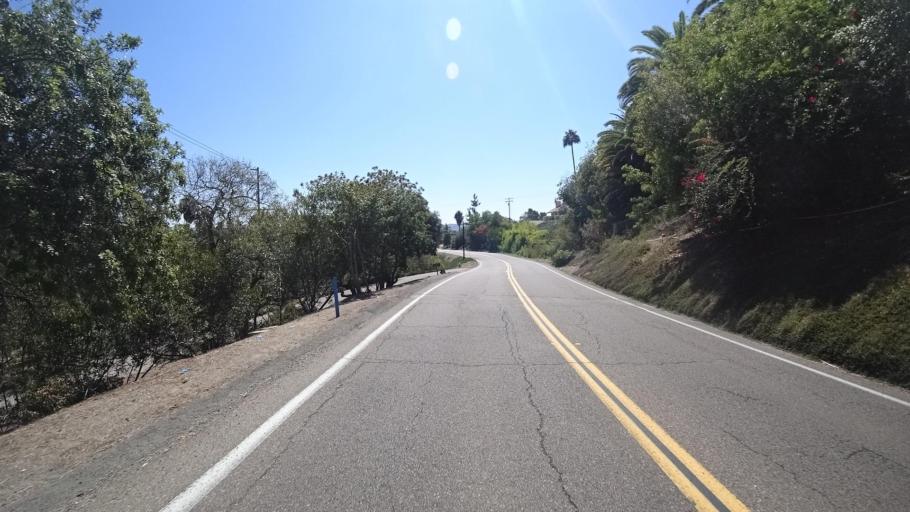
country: US
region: California
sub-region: San Diego County
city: Rancho Santa Fe
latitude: 33.0174
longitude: -117.1989
